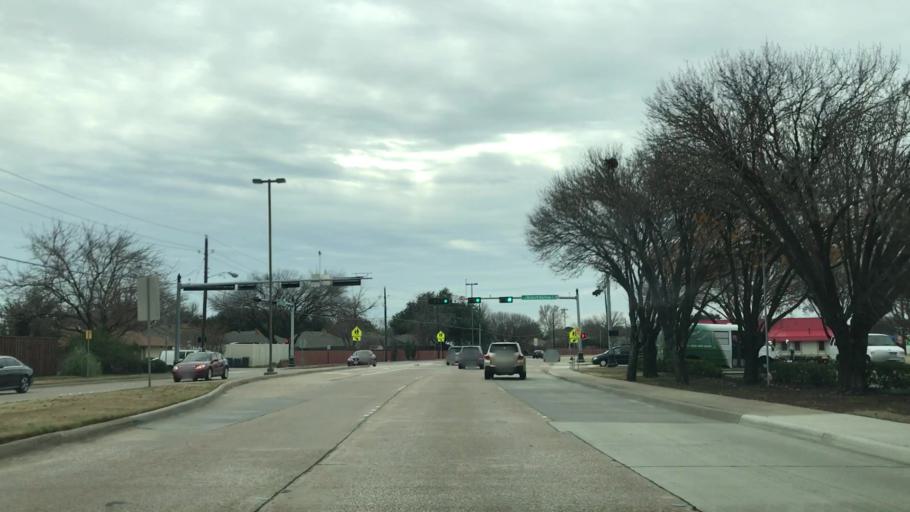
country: US
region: Texas
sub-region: Dallas County
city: Carrollton
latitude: 33.0202
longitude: -96.8850
